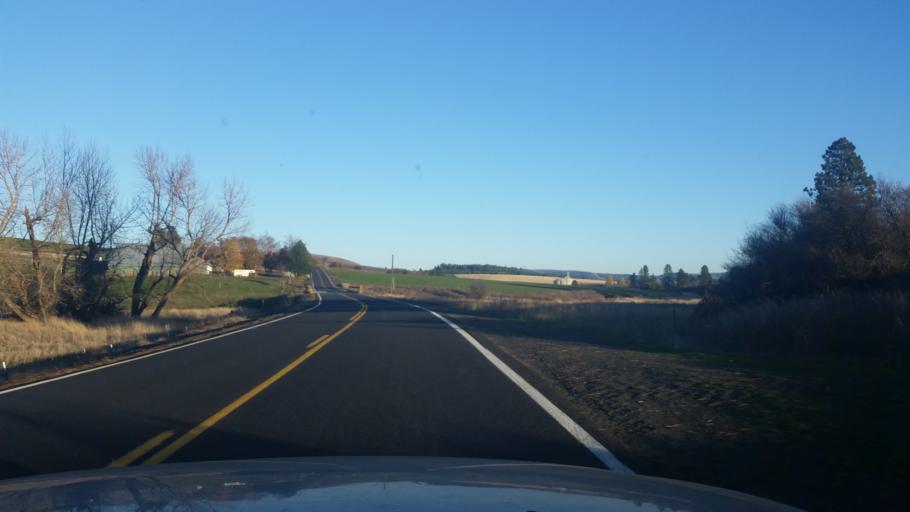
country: US
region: Washington
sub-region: Spokane County
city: Opportunity
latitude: 47.3514
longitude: -117.2486
